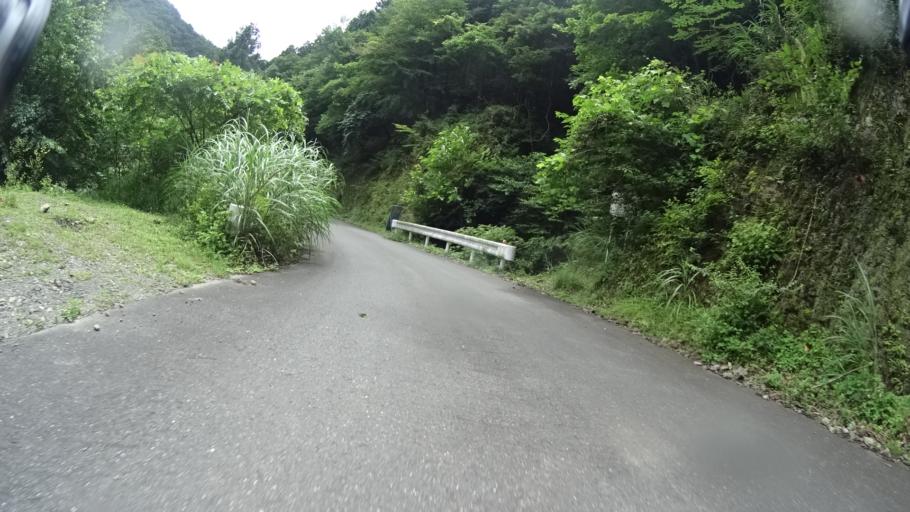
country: JP
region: Saitama
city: Chichibu
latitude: 35.8812
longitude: 139.1419
